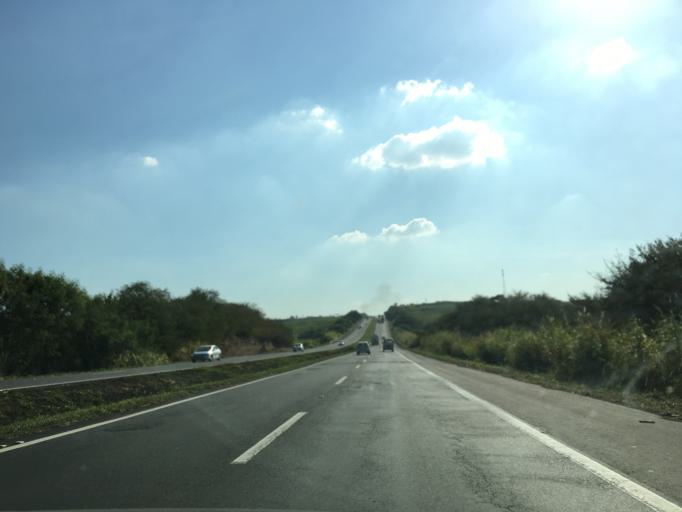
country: BR
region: Sao Paulo
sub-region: Santa Barbara D'Oeste
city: Santa Barbara d'Oeste
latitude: -22.7528
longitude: -47.4878
